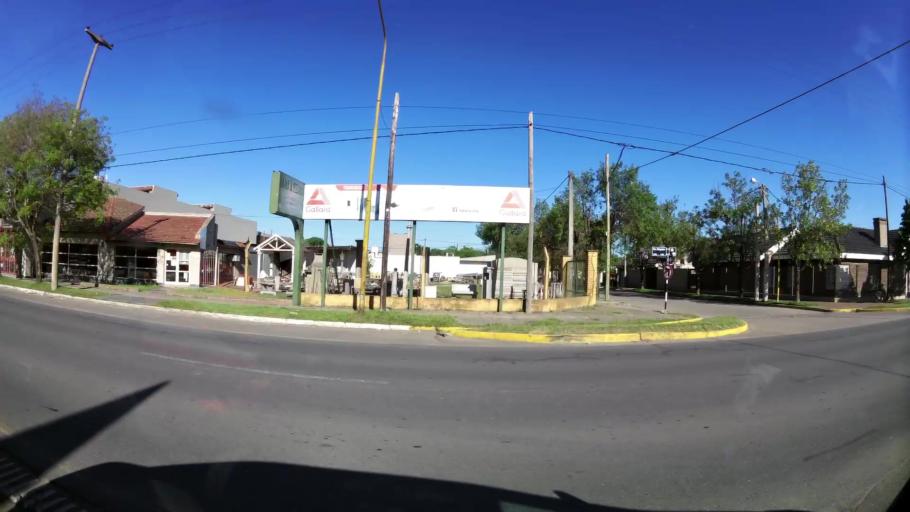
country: AR
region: Cordoba
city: San Francisco
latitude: -31.4176
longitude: -62.0947
